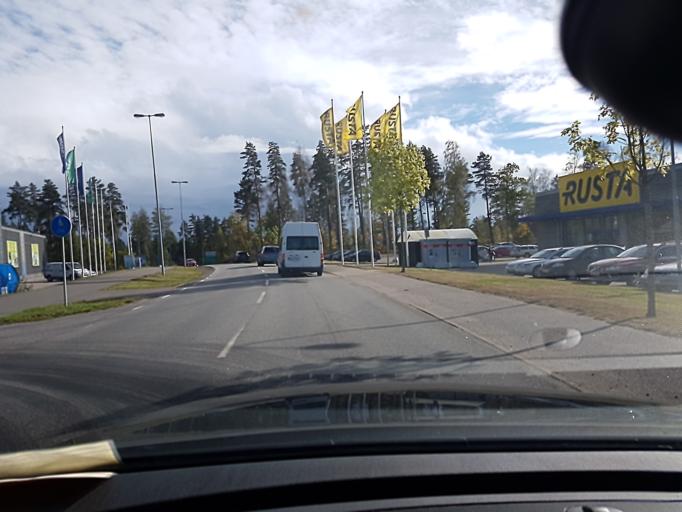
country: SE
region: Kronoberg
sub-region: Vaxjo Kommun
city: Vaexjoe
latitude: 56.8814
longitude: 14.7637
